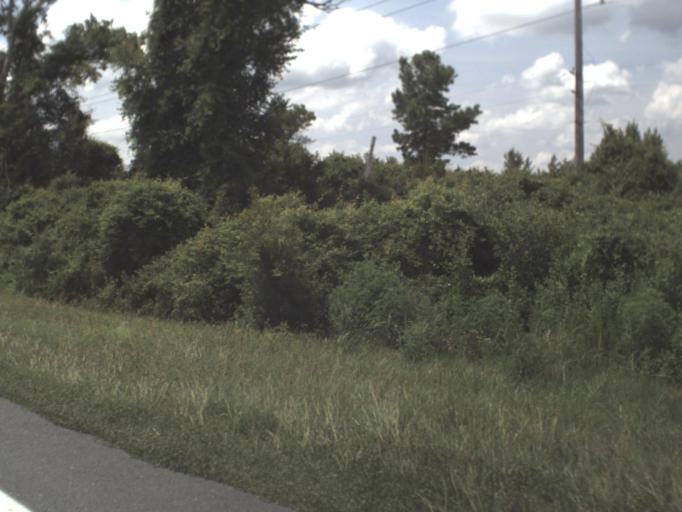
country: US
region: Florida
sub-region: Hamilton County
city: Jasper
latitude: 30.4529
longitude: -82.8890
